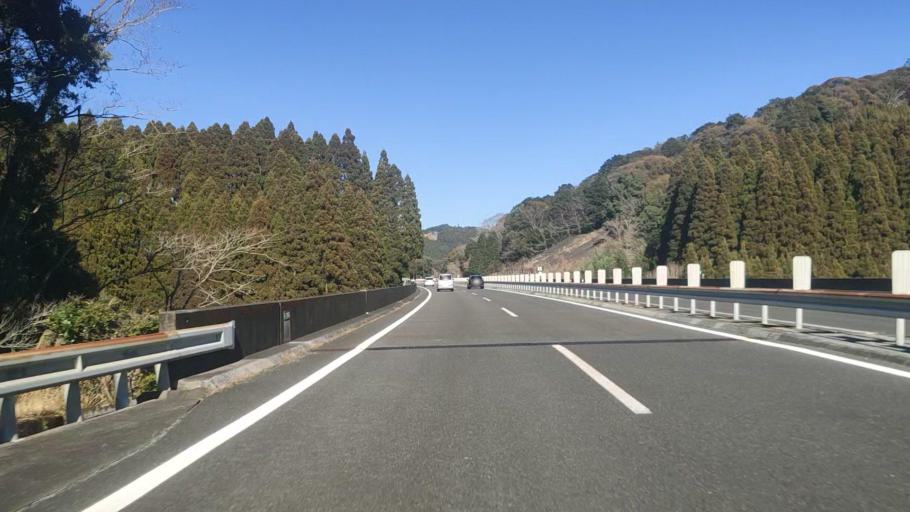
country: JP
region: Miyazaki
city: Miyakonojo
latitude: 31.8132
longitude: 131.2155
